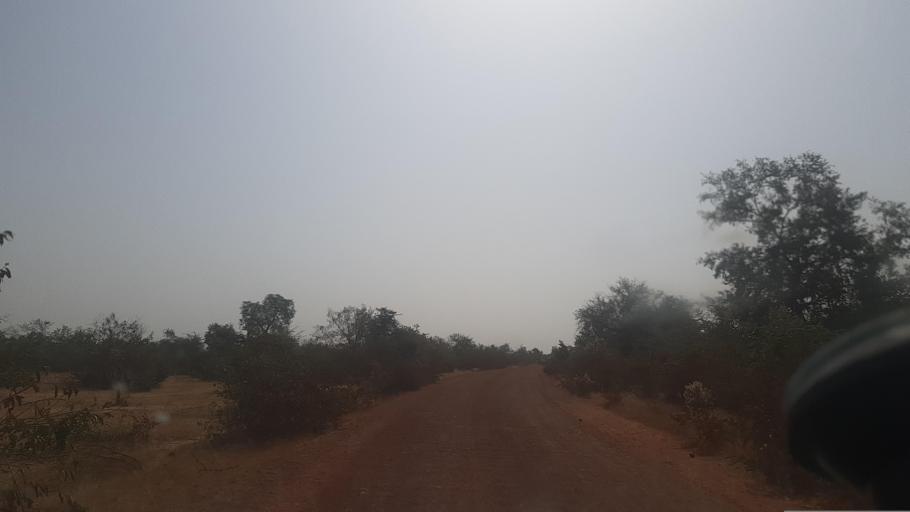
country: ML
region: Segou
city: Baroueli
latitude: 13.0642
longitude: -6.4753
